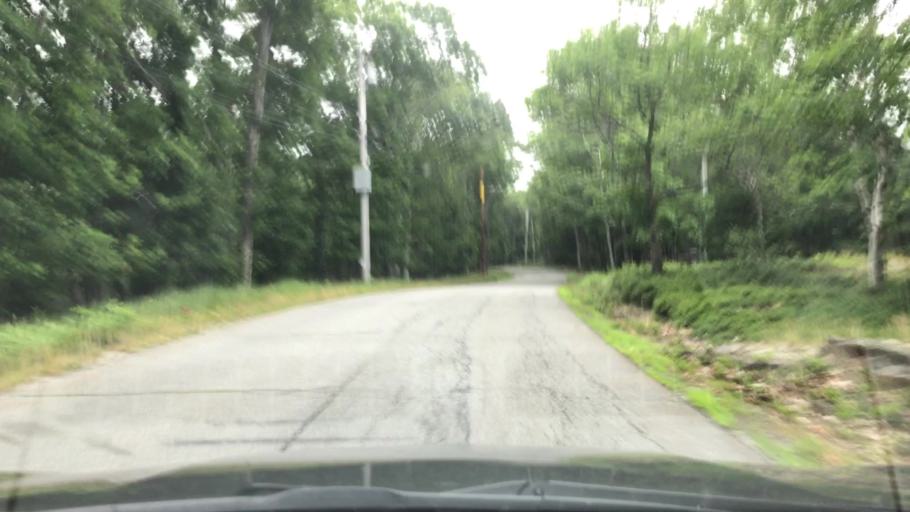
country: US
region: Maine
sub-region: Hancock County
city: Bar Harbor
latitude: 44.3442
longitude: -68.1796
